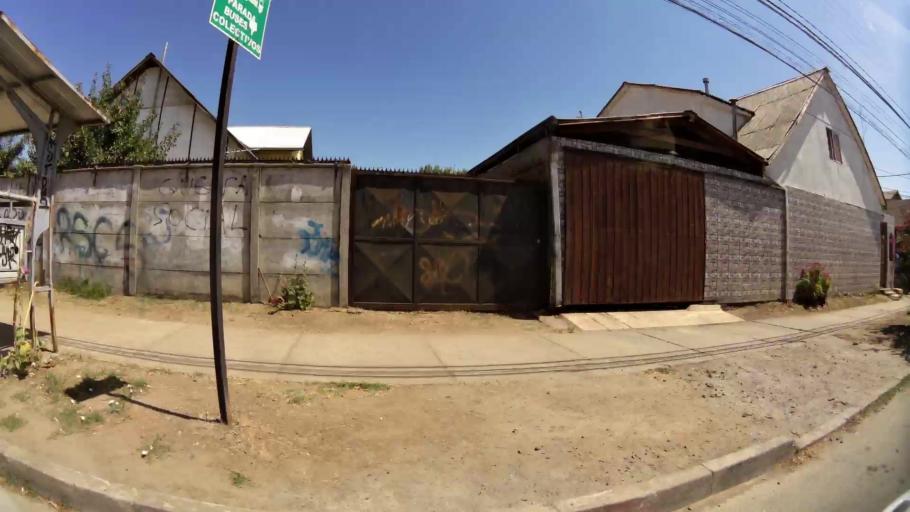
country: CL
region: Maule
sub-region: Provincia de Talca
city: Talca
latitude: -35.4269
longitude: -71.6260
